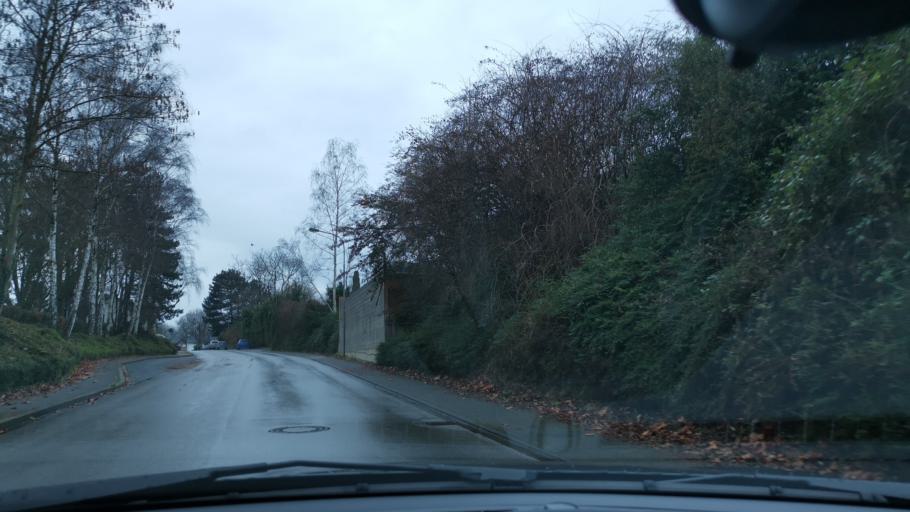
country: DE
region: North Rhine-Westphalia
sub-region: Regierungsbezirk Koln
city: Bedburg
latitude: 50.9895
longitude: 6.5664
